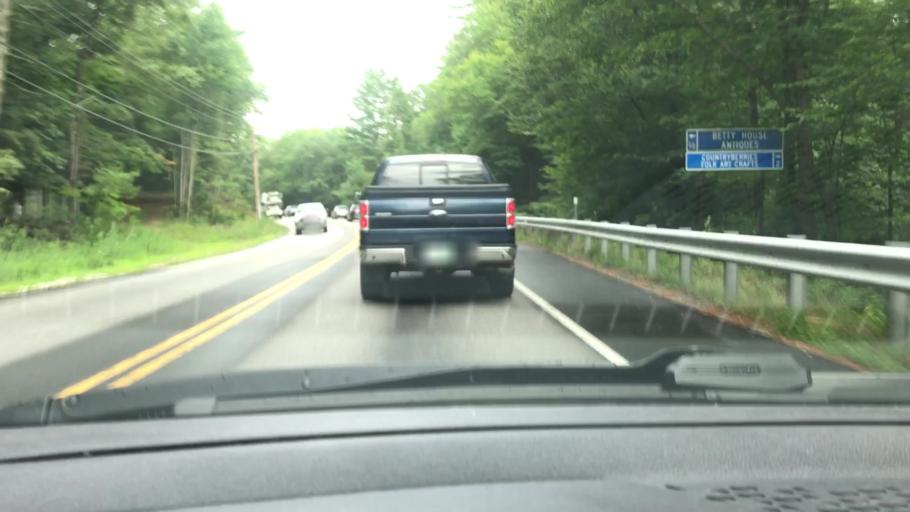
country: US
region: New Hampshire
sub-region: Merrimack County
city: Epsom
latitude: 43.2215
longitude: -71.2969
